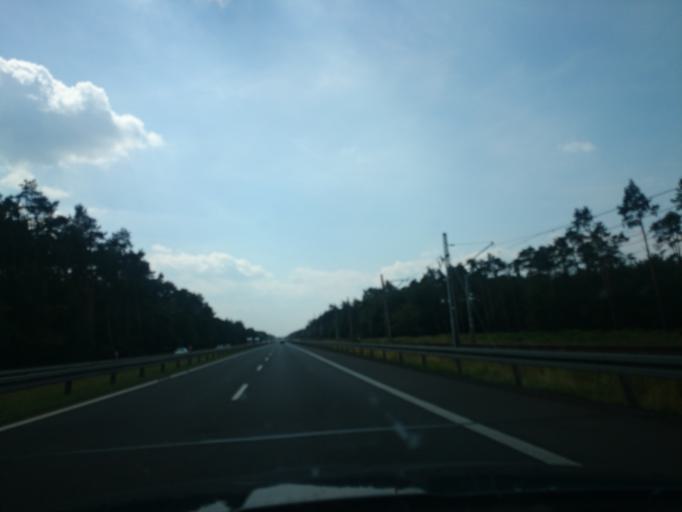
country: PL
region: West Pomeranian Voivodeship
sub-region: Powiat goleniowski
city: Goleniow
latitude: 53.4990
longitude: 14.7982
